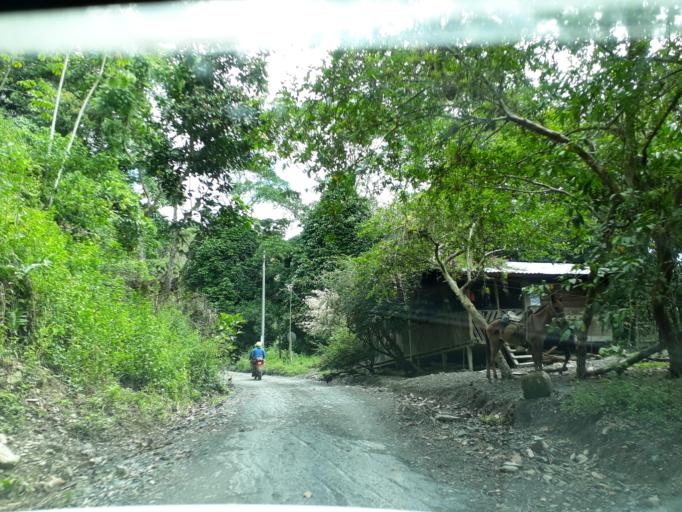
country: CO
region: Boyaca
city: Quipama
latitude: 5.4500
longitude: -74.1755
